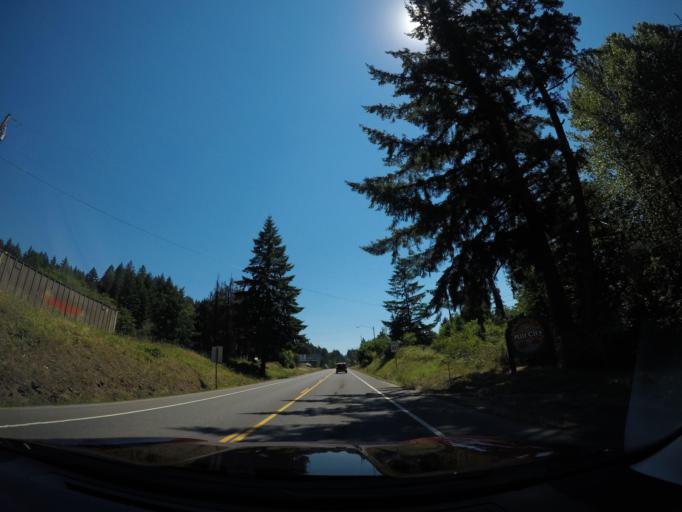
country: US
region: Oregon
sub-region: Linn County
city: Mill City
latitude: 44.7574
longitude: -122.4904
